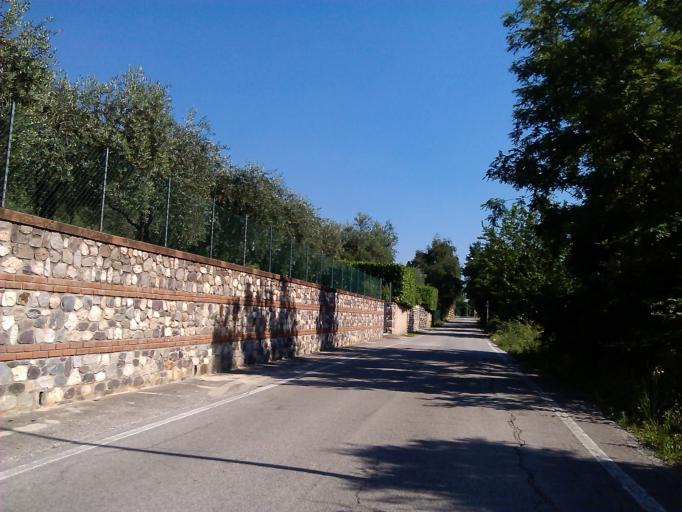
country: IT
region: Veneto
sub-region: Provincia di Vicenza
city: Pove del Grappa
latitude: 45.7974
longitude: 11.7254
